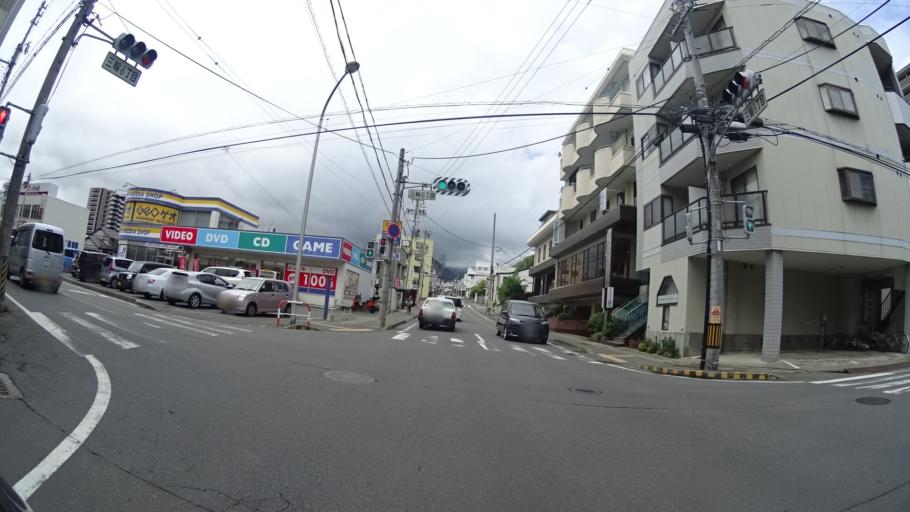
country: JP
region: Nagano
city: Nagano-shi
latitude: 36.6588
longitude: 138.1946
